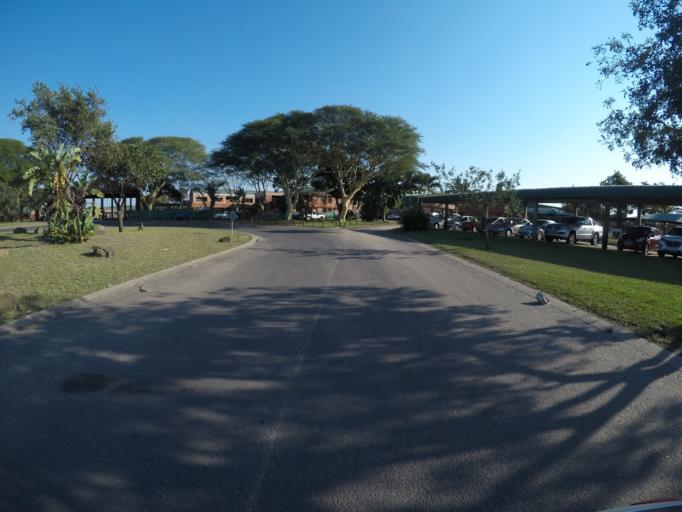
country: ZA
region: KwaZulu-Natal
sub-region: uThungulu District Municipality
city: Richards Bay
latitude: -28.7470
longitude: 32.0187
